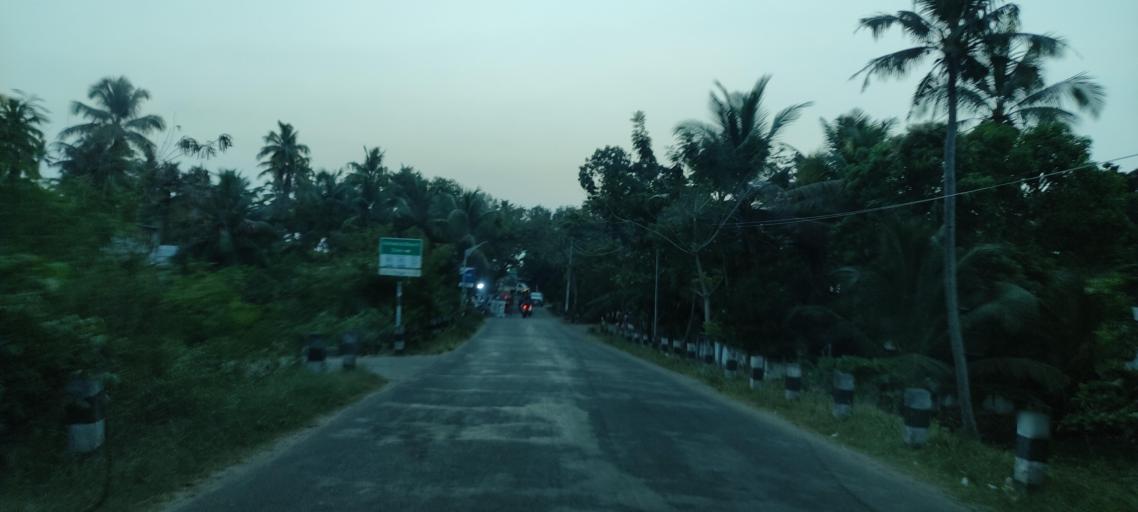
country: IN
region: Kerala
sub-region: Alappuzha
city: Kayankulam
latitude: 9.1145
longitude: 76.4748
